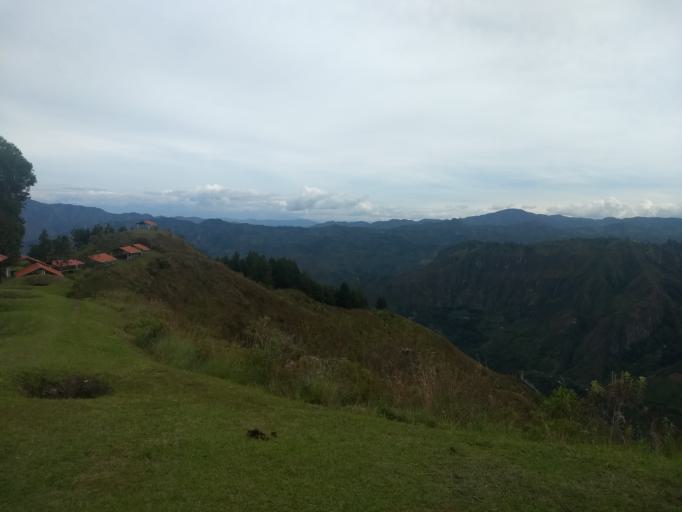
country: CO
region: Cauca
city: Inza
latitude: 2.5678
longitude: -76.0504
